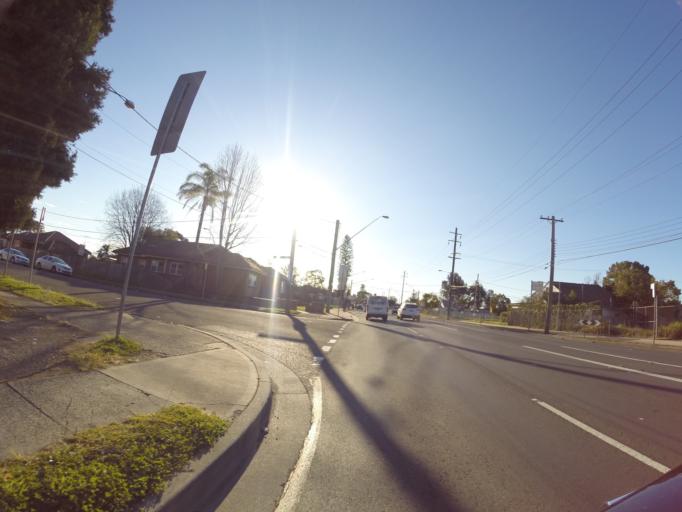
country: AU
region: New South Wales
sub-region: Fairfield
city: Fairfield Heights
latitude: -33.8652
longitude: 150.9551
